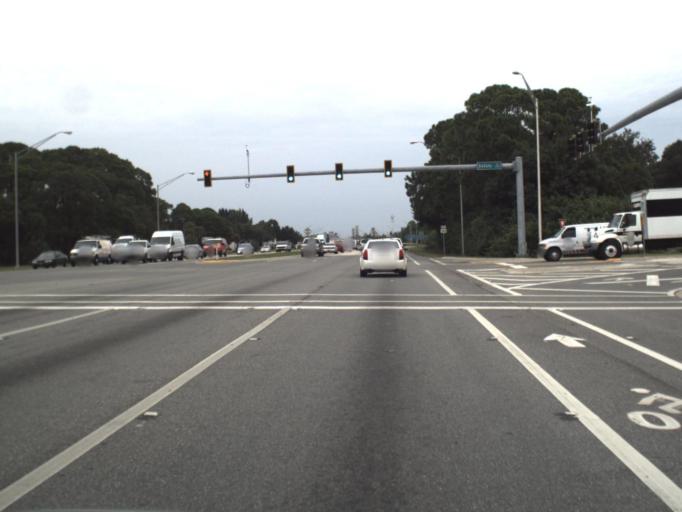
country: US
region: Florida
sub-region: Sarasota County
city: North Sarasota
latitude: 27.3812
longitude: -82.5307
